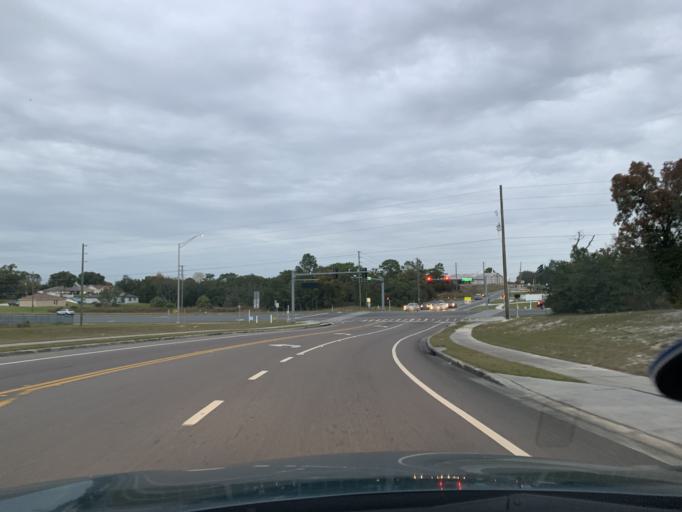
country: US
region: Florida
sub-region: Hernando County
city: Timber Pines
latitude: 28.4329
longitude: -82.6020
